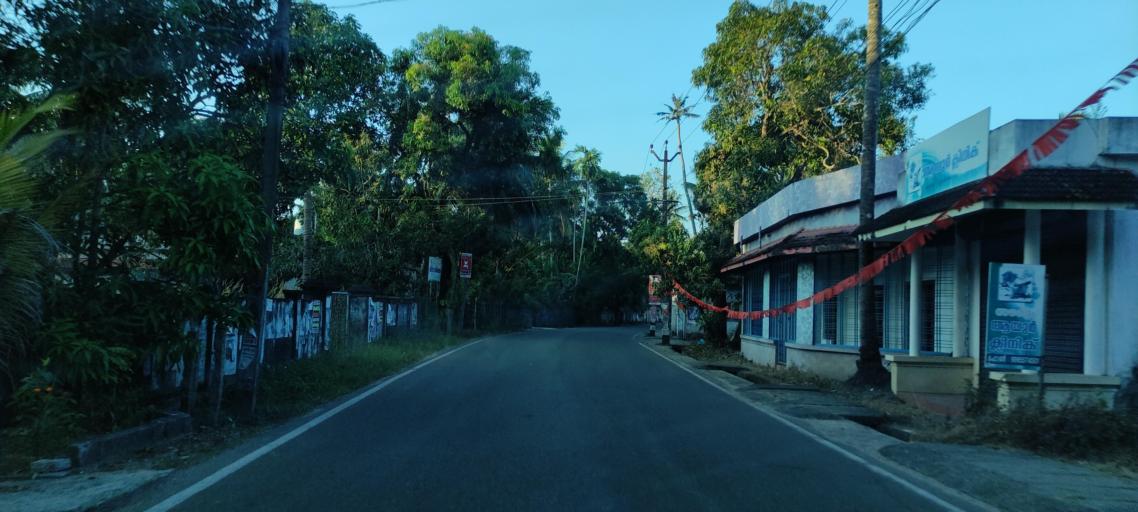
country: IN
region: Kerala
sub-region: Alappuzha
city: Kayankulam
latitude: 9.1871
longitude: 76.4718
